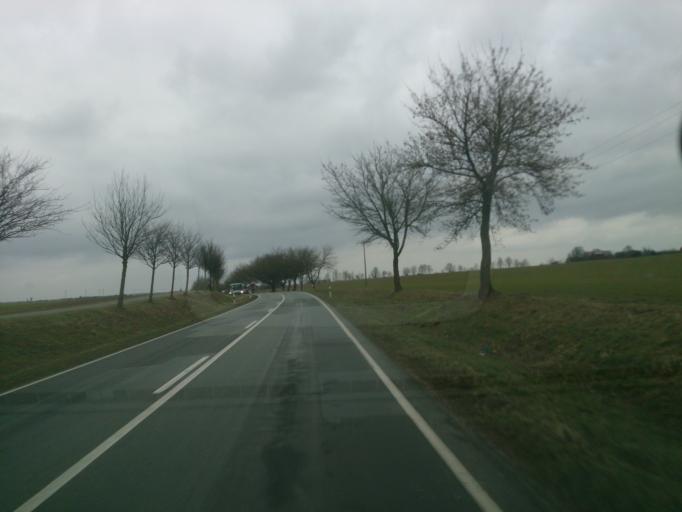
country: DE
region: Mecklenburg-Vorpommern
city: Wackerow
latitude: 53.6750
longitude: 12.9063
